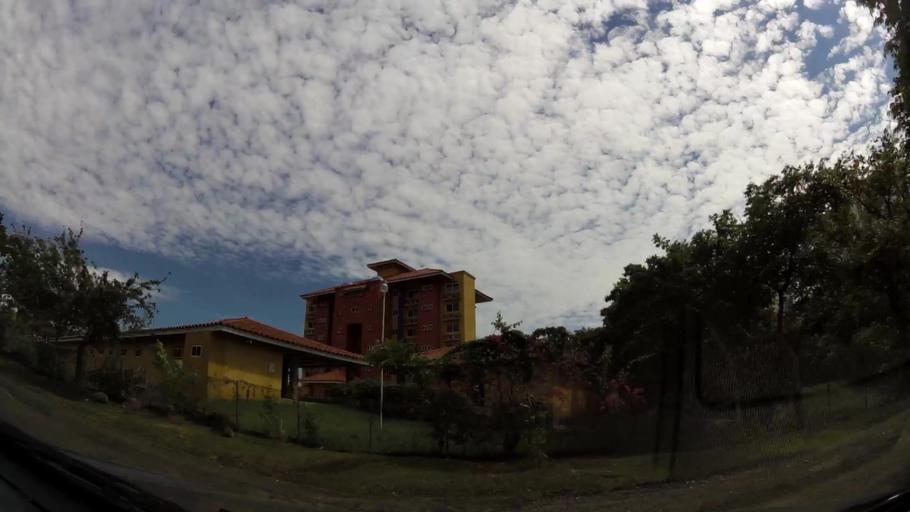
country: PA
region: Panama
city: Nueva Gorgona
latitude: 8.5197
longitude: -79.9138
